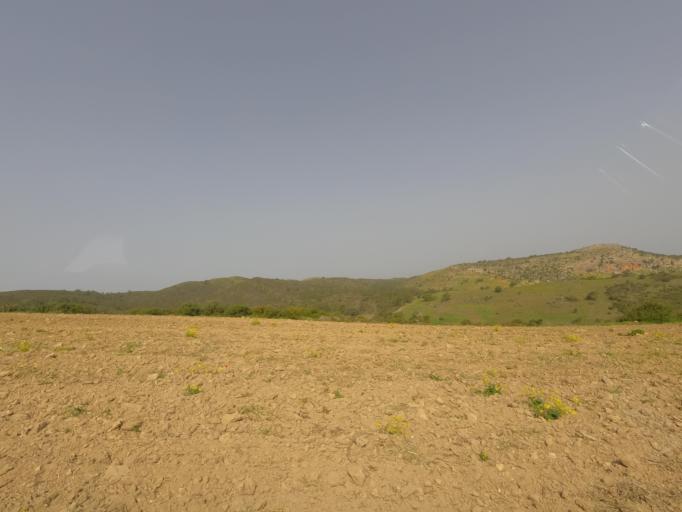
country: CY
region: Pafos
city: Polis
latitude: 35.0051
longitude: 32.3502
